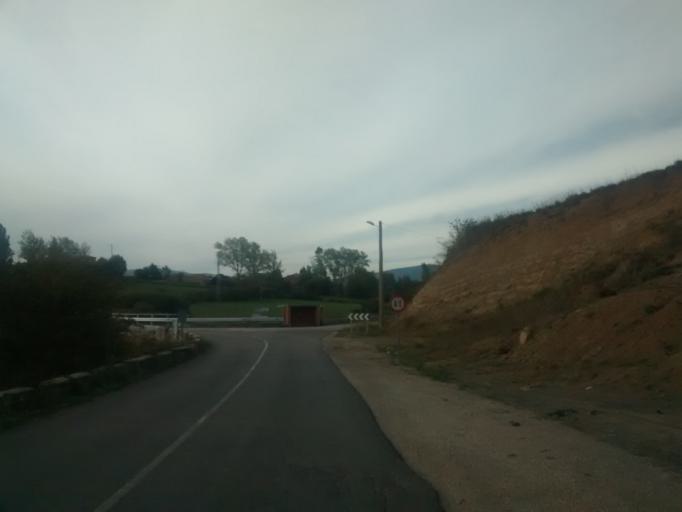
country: ES
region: Castille and Leon
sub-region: Provincia de Burgos
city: Arija
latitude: 42.9851
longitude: -3.9527
